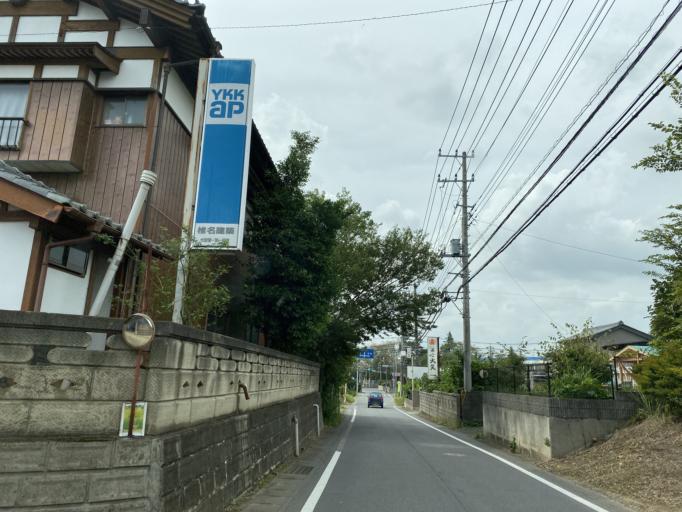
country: JP
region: Ibaraki
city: Mitsukaido
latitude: 36.0415
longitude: 140.0450
